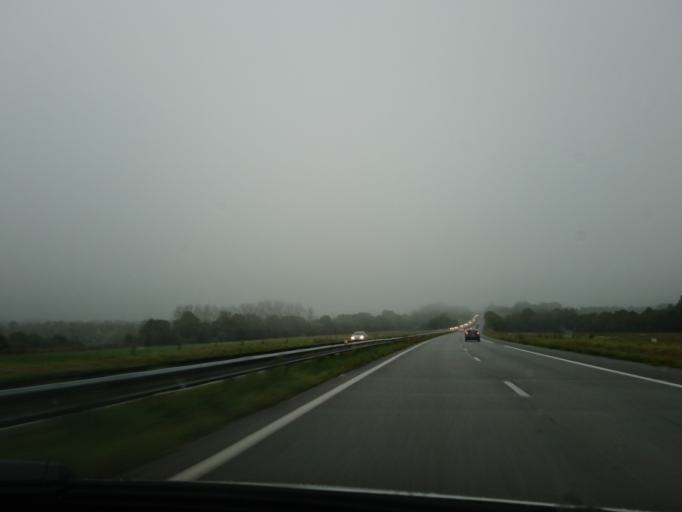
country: FR
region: Brittany
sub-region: Departement du Finistere
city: Landrevarzec
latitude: 48.0680
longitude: -4.0484
